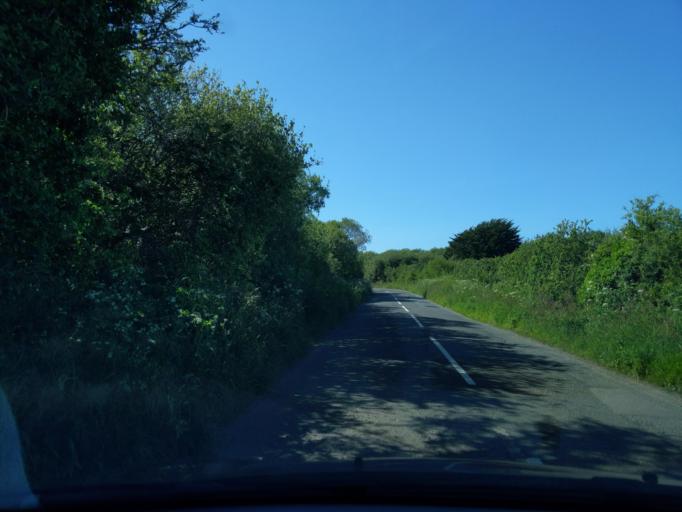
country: GB
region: England
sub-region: Cornwall
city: St. Buryan
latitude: 50.0598
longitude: -5.6263
